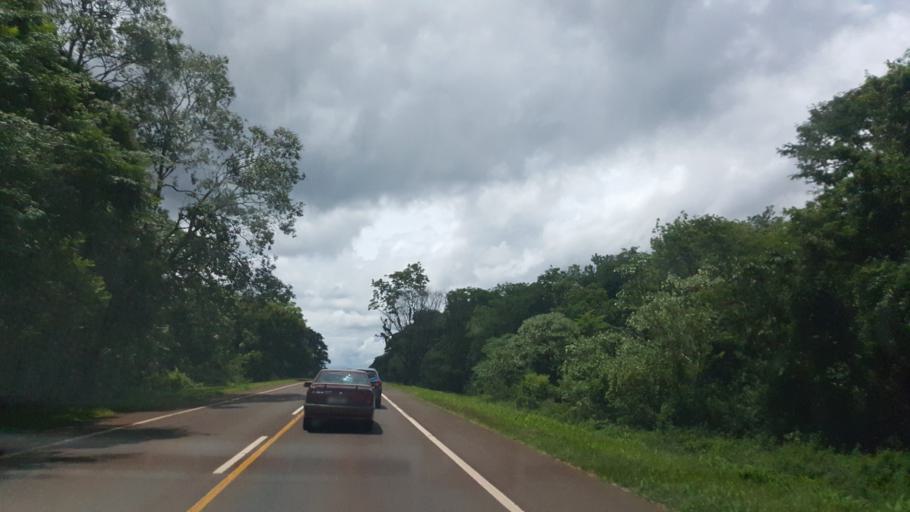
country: AR
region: Misiones
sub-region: Departamento de Iguazu
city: Puerto Iguazu
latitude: -25.6983
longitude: -54.5148
